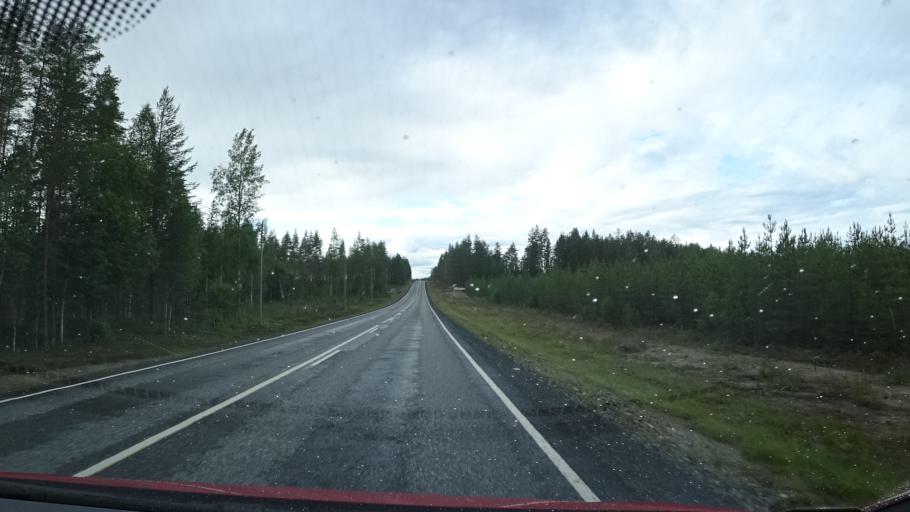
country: FI
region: Kainuu
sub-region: Kehys-Kainuu
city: Kuhmo
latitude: 64.0936
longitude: 29.4790
